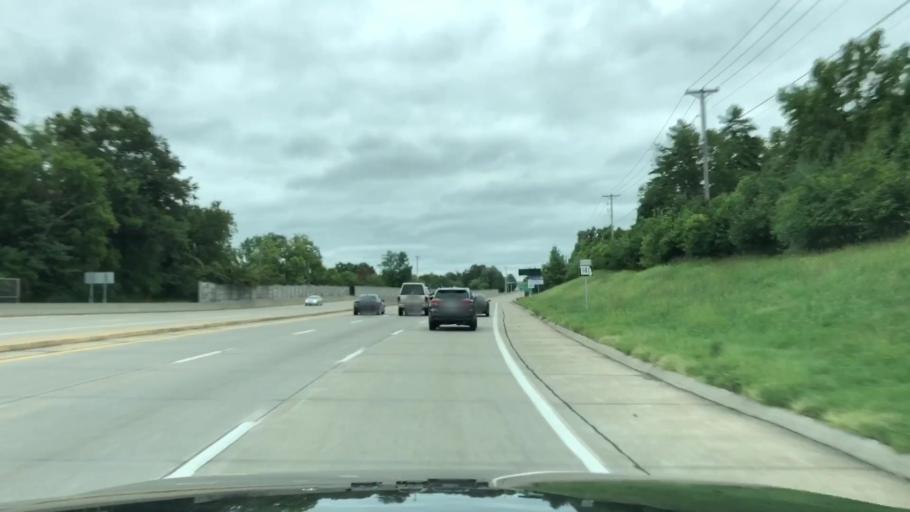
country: US
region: Missouri
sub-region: Saint Louis County
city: Manchester
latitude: 38.6084
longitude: -90.5110
